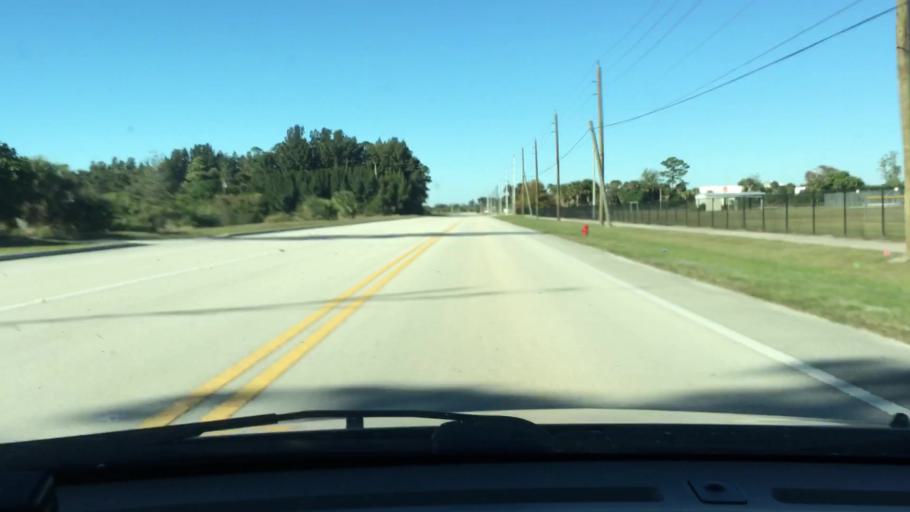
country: US
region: Florida
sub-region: Indian River County
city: Winter Beach
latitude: 27.6973
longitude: -80.4551
